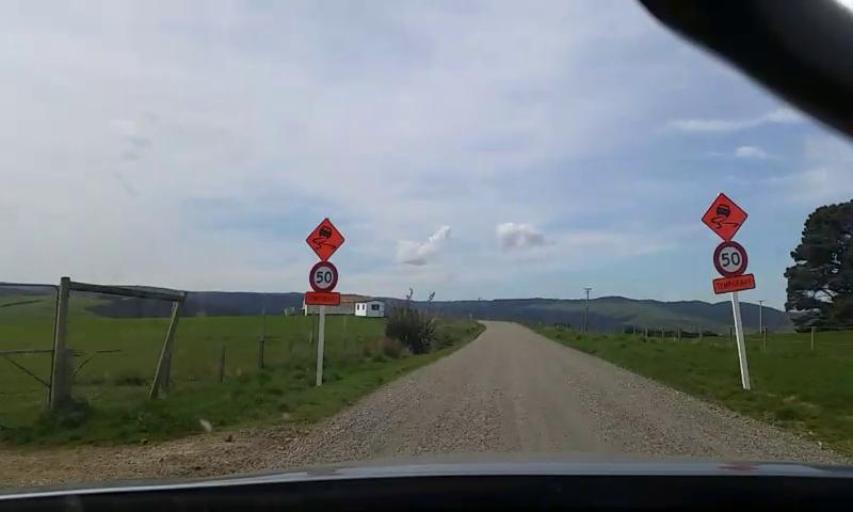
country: NZ
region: Otago
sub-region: Clutha District
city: Papatowai
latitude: -46.6313
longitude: 168.9792
